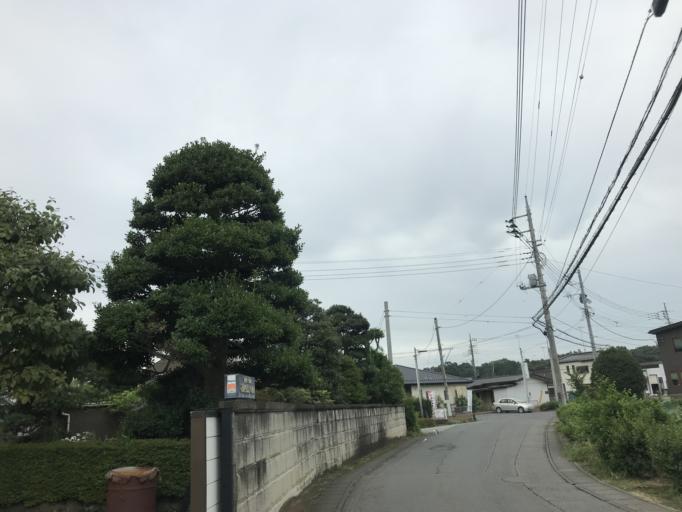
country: JP
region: Ibaraki
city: Sakai
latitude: 36.1559
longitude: 139.7748
